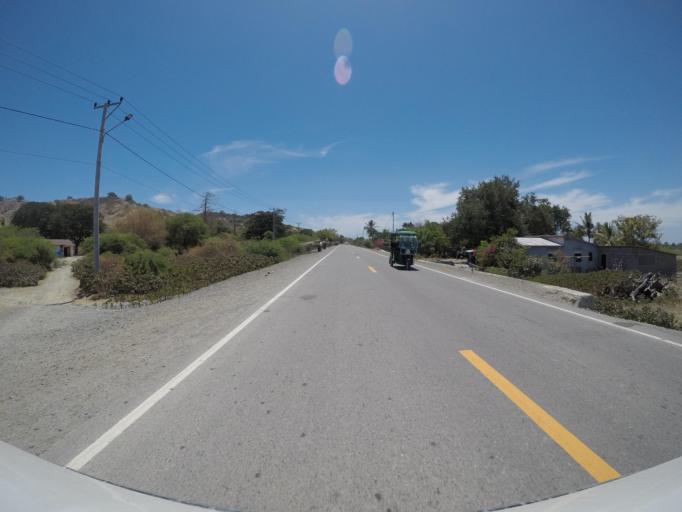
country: TL
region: Manatuto
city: Manatuto
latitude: -8.5085
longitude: 125.9959
